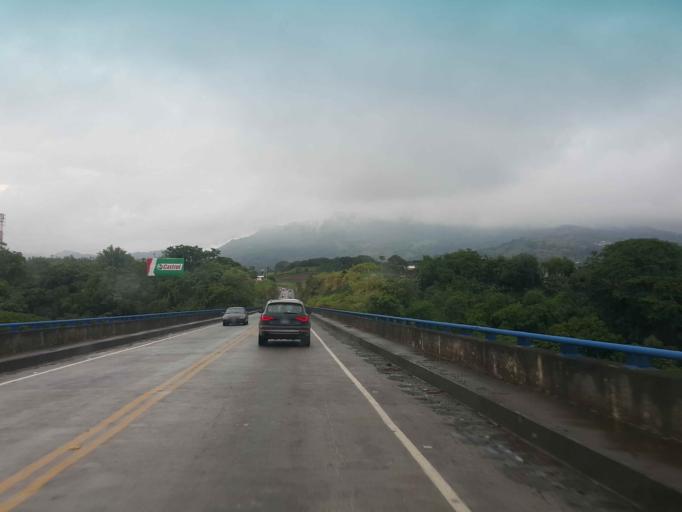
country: CR
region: Heredia
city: Colon
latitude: 9.9479
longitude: -84.2327
